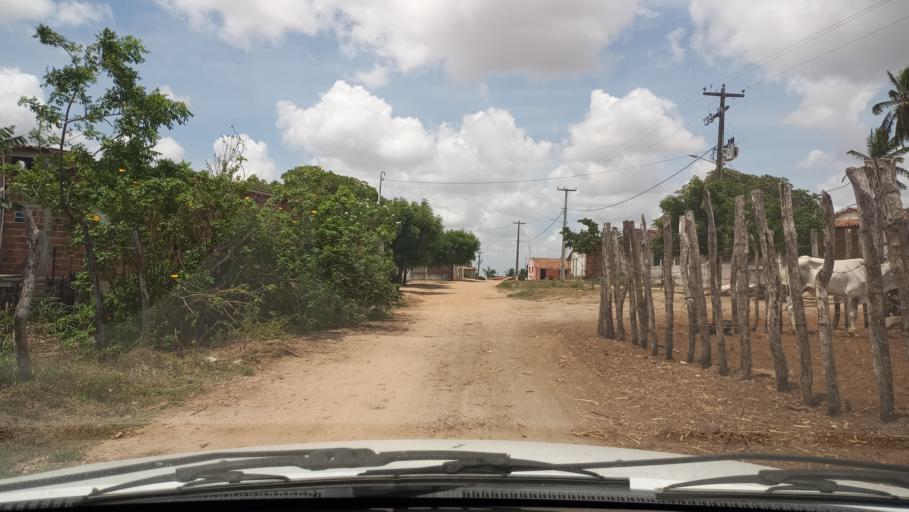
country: BR
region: Rio Grande do Norte
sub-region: Brejinho
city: Brejinho
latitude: -6.2858
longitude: -35.3537
